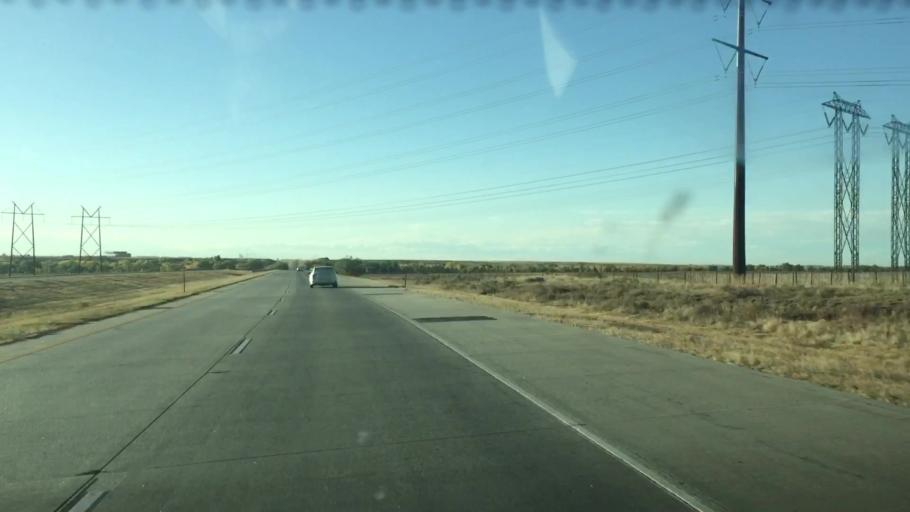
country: US
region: Colorado
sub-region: Arapahoe County
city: Byers
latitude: 39.6657
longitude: -104.0881
